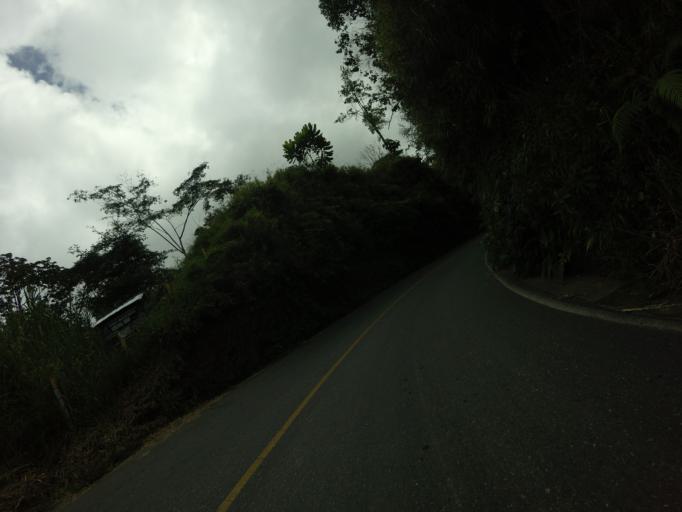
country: CO
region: Caldas
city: Marquetalia
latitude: 5.3077
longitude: -75.0038
